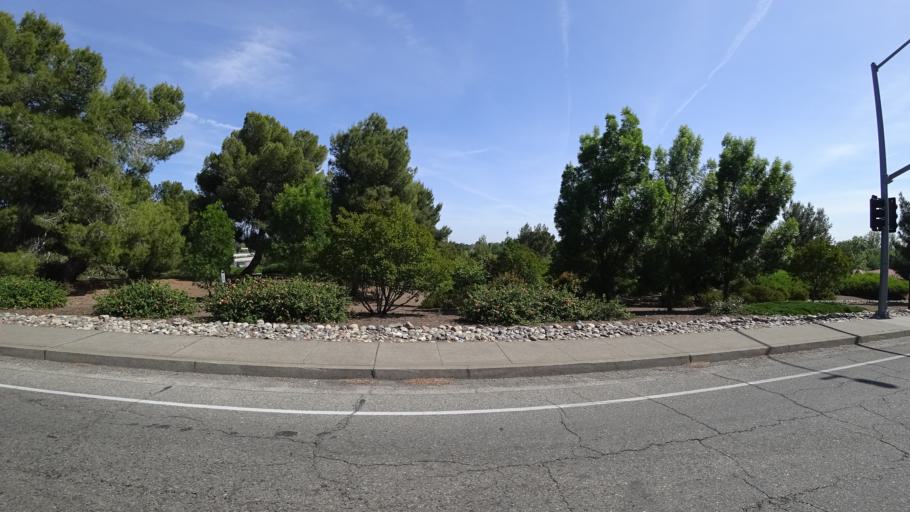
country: US
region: California
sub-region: Tehama County
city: Red Bluff
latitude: 40.1800
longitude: -122.2265
